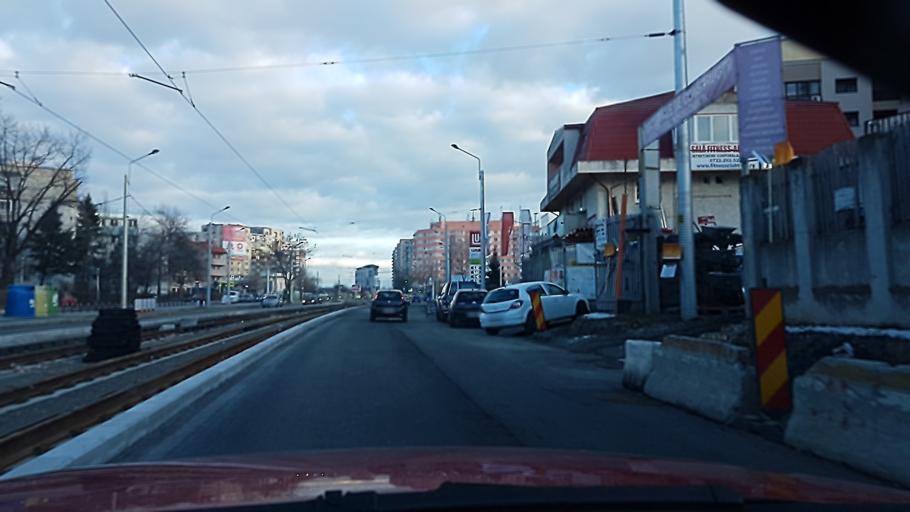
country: RO
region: Ilfov
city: Dobroesti
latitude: 44.4243
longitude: 26.1739
